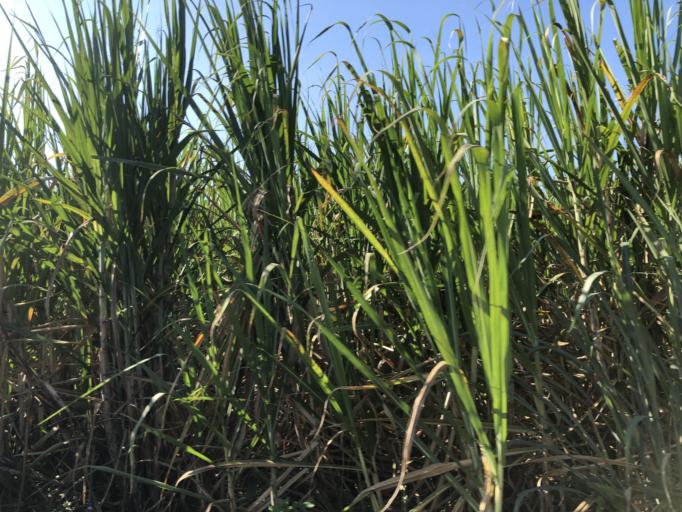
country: TW
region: Taiwan
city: Yujing
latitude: 23.0462
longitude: 120.4012
